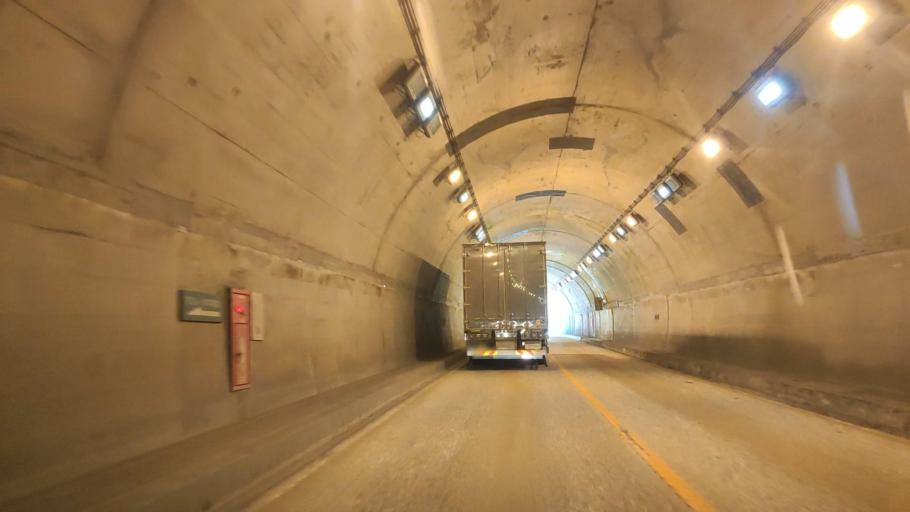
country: JP
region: Aomori
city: Aomori Shi
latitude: 40.7829
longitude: 141.0584
